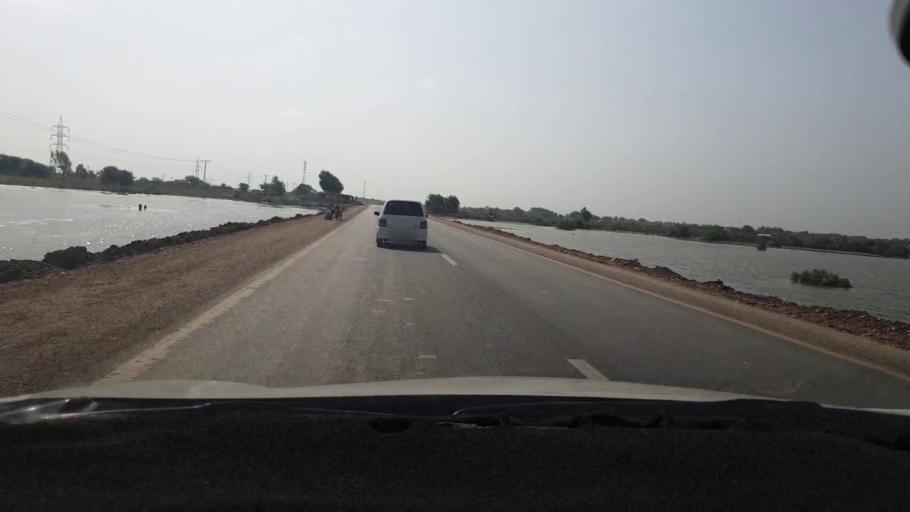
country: PK
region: Sindh
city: Jhol
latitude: 25.8918
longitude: 69.0294
